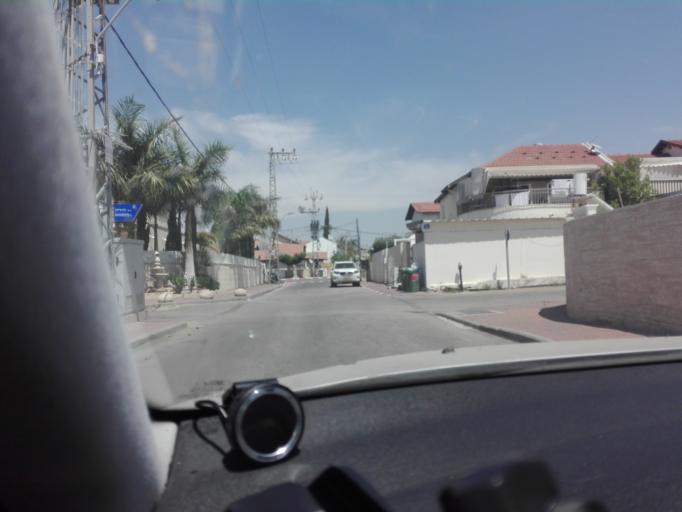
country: IL
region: Central District
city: Bene 'Ayish
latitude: 31.7330
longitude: 34.7466
